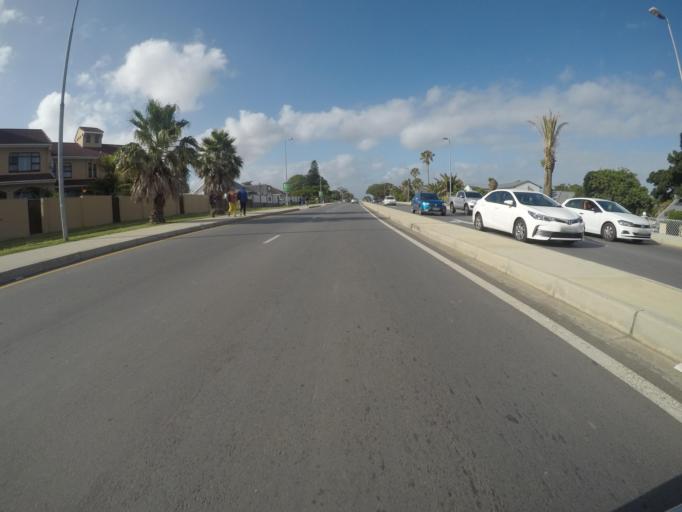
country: ZA
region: Eastern Cape
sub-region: Buffalo City Metropolitan Municipality
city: East London
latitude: -32.9633
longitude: 27.9343
